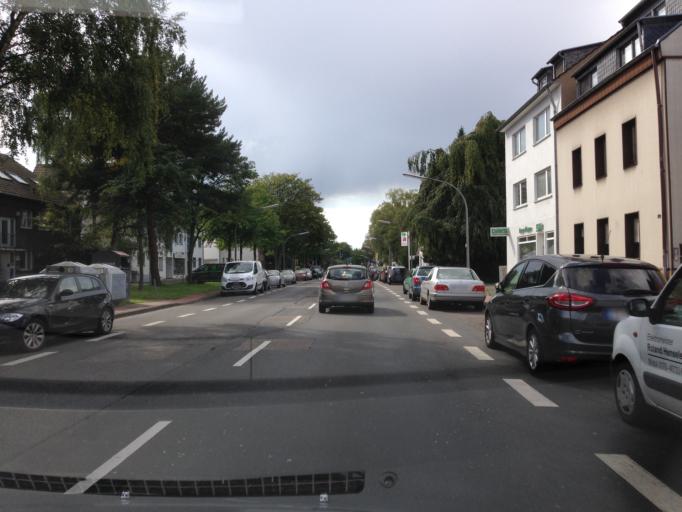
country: DE
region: North Rhine-Westphalia
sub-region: Regierungsbezirk Koln
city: Eil
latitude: 50.8924
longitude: 7.0721
